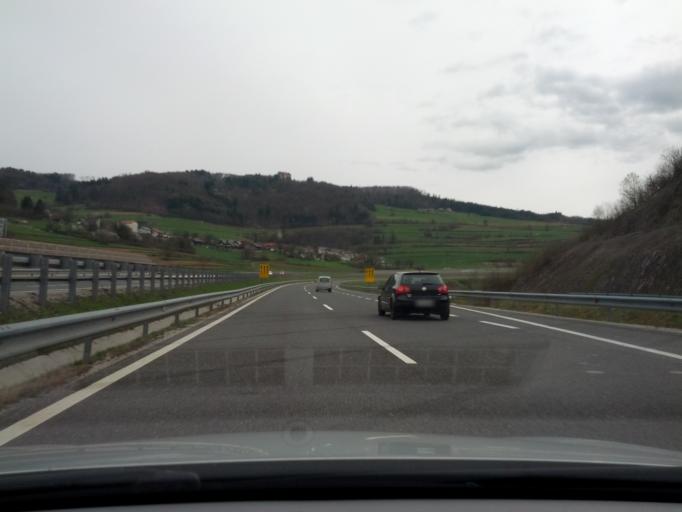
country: SI
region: Mirna Pec
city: Mirna Pec
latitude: 45.8641
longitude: 15.1313
